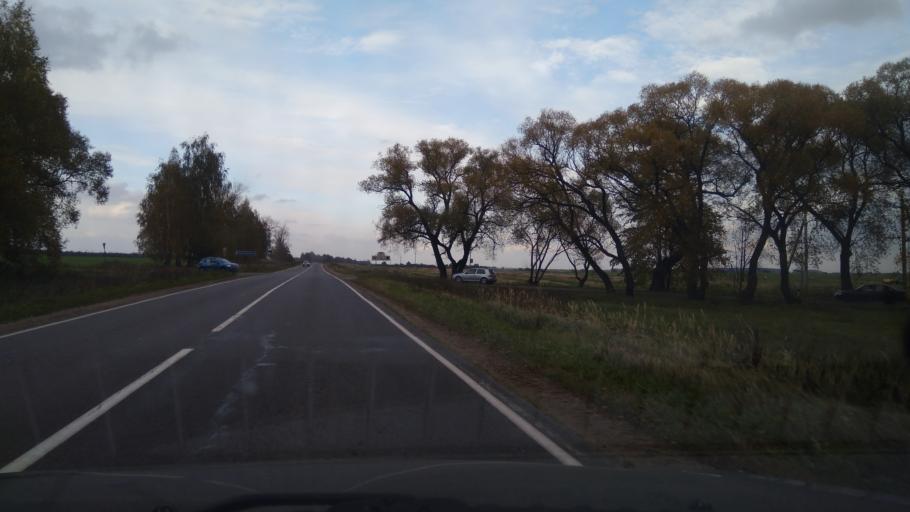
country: BY
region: Minsk
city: Dukora
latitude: 53.6809
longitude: 27.9567
